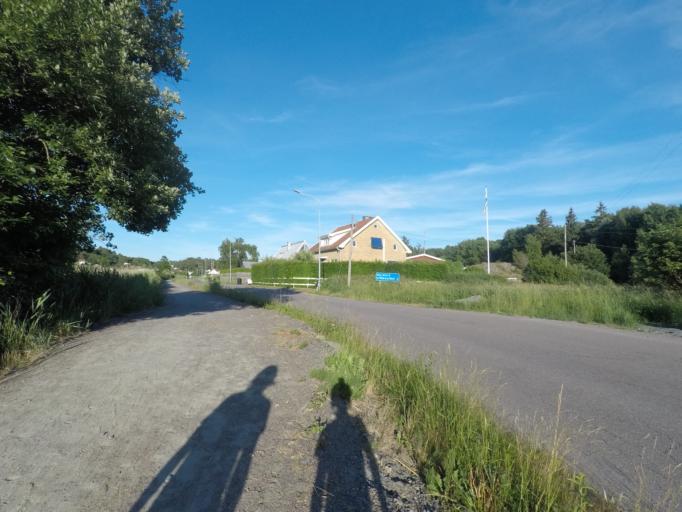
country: SE
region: Vaestra Goetaland
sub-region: Goteborg
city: Billdal
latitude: 57.5802
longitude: 11.9518
